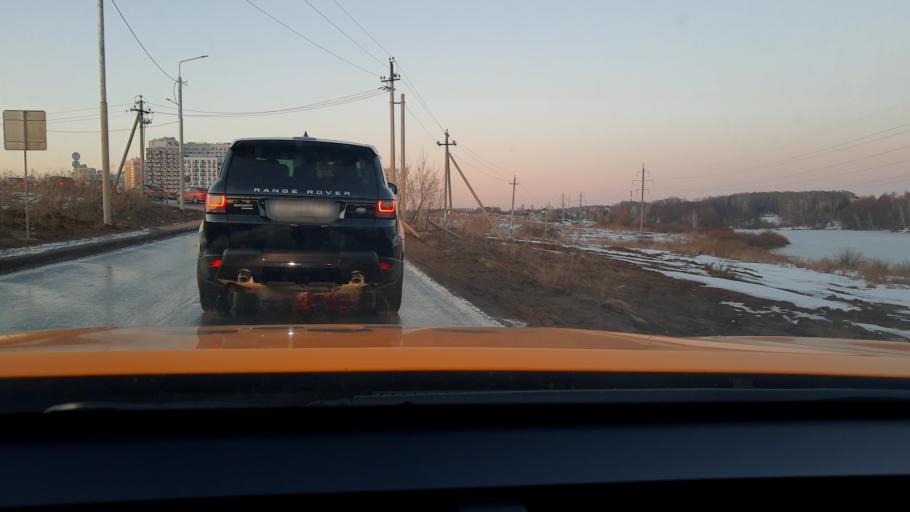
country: RU
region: Moskovskaya
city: Vidnoye
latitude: 55.5251
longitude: 37.7191
